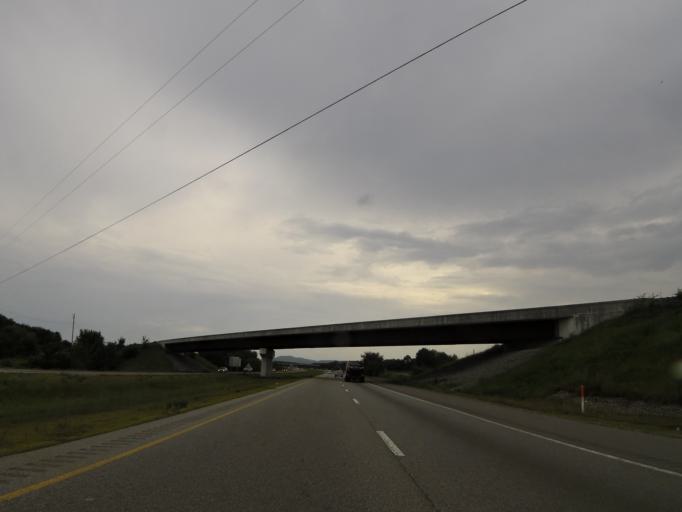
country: US
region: Tennessee
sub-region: Rutherford County
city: Murfreesboro
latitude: 35.8719
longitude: -86.4995
